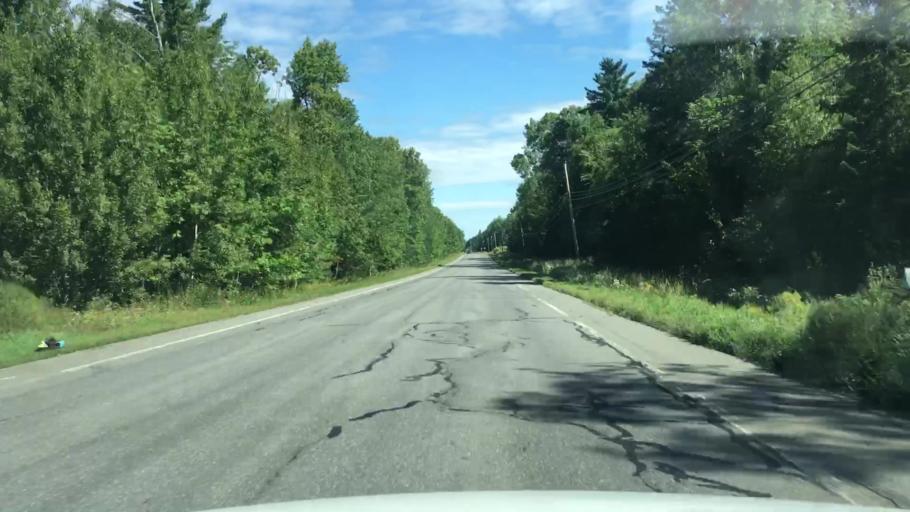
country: US
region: Maine
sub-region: Penobscot County
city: Dexter
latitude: 45.0632
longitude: -69.2465
